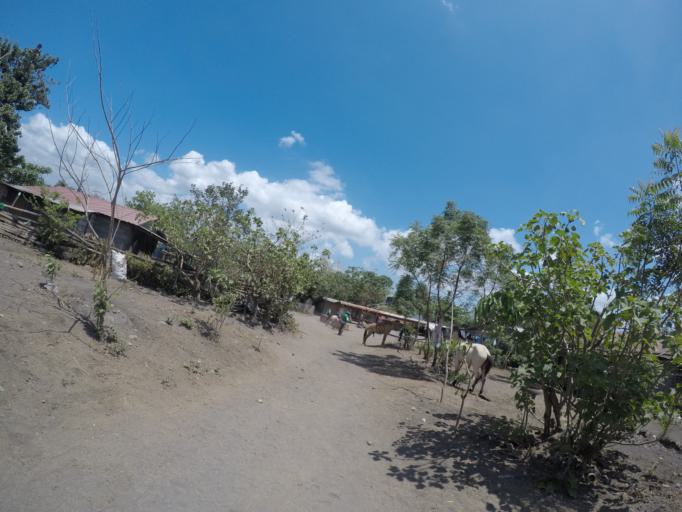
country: PH
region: Calabarzon
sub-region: Province of Batangas
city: Talisay
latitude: 14.0341
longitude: 121.0026
